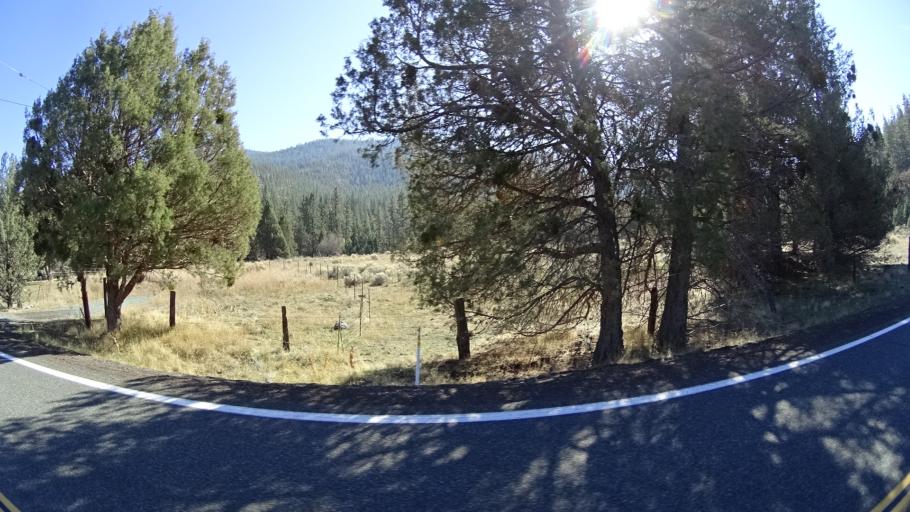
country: US
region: California
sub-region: Siskiyou County
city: Weed
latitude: 41.4728
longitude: -122.5817
